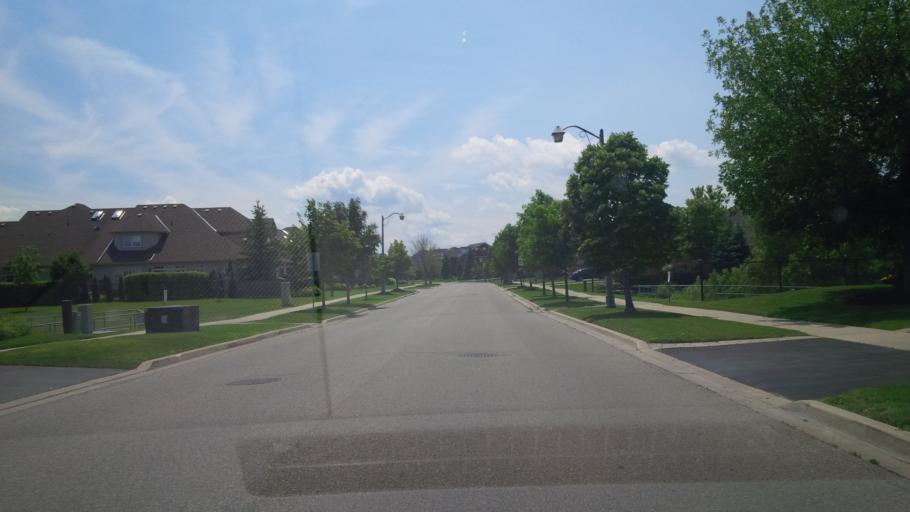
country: CA
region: Ontario
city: Burlington
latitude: 43.4013
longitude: -79.8067
